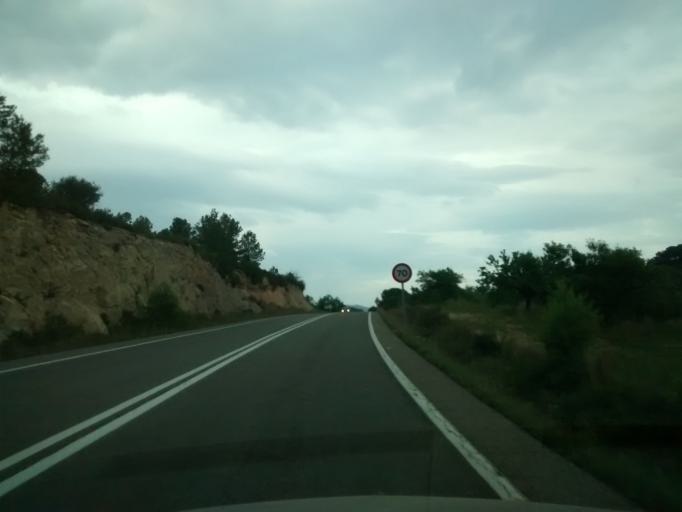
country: ES
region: Catalonia
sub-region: Provincia de Tarragona
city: Benifallet
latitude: 41.0102
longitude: 0.5039
